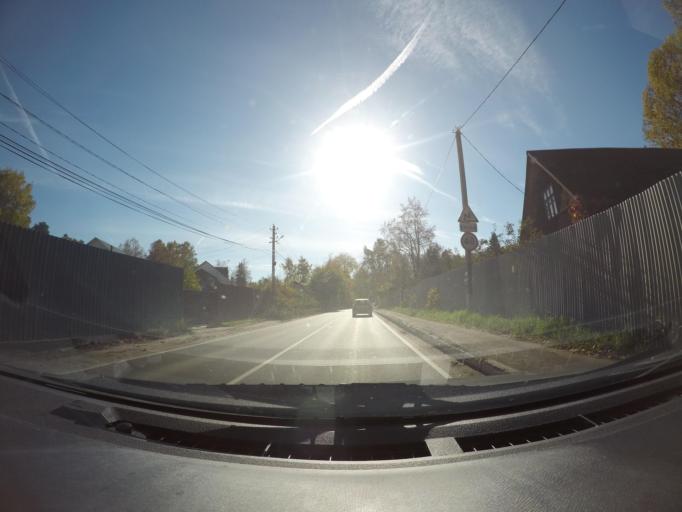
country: RU
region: Moskovskaya
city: Rodniki
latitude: 55.6420
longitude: 38.0529
